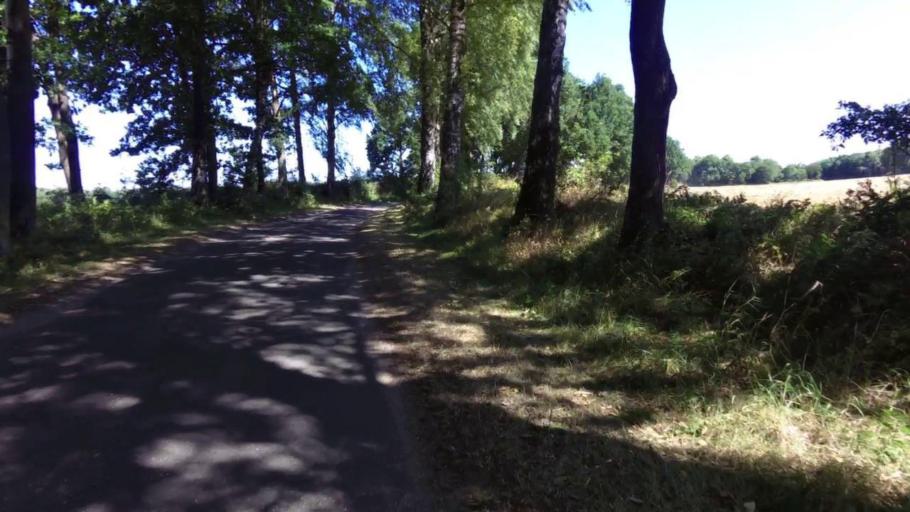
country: PL
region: West Pomeranian Voivodeship
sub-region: Powiat drawski
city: Czaplinek
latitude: 53.5255
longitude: 16.2021
